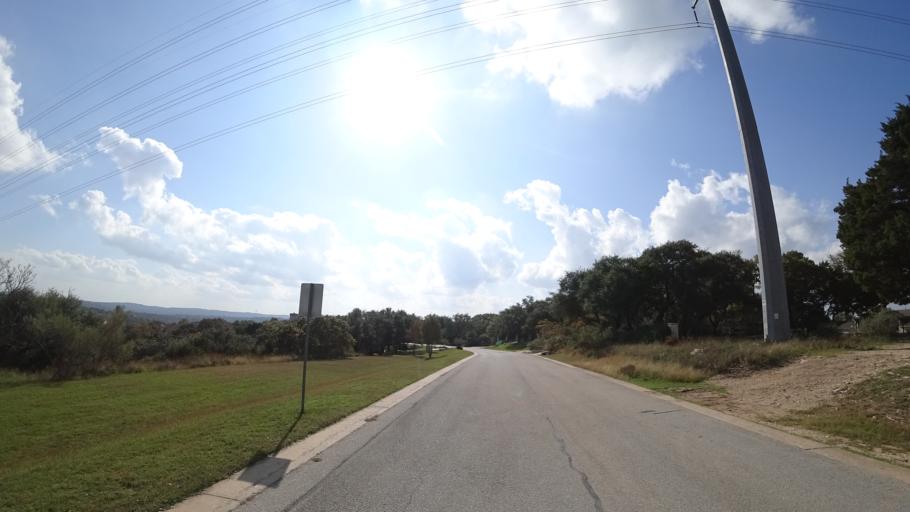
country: US
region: Texas
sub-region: Travis County
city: Lost Creek
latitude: 30.3057
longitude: -97.8502
